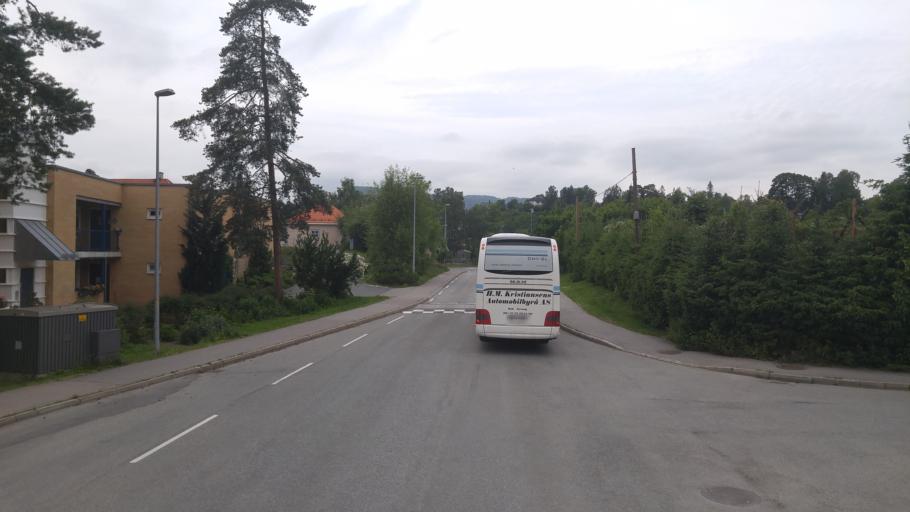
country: NO
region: Akershus
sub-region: Baerum
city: Sandvika
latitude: 59.8921
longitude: 10.5565
